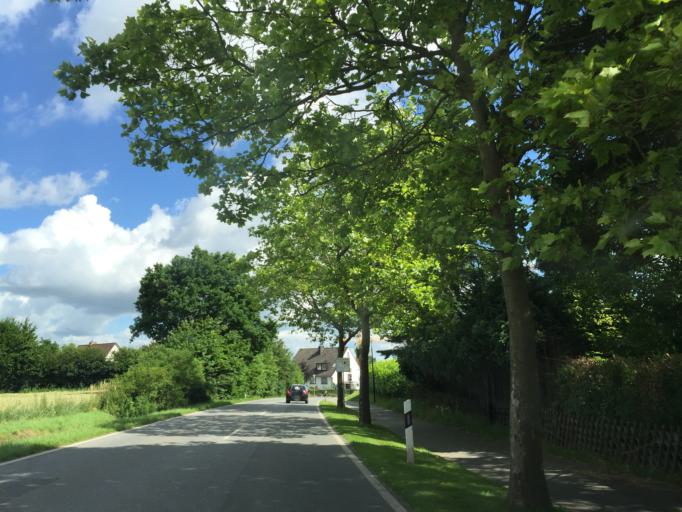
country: DE
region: Schleswig-Holstein
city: Scharbeutz
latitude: 54.0179
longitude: 10.7397
